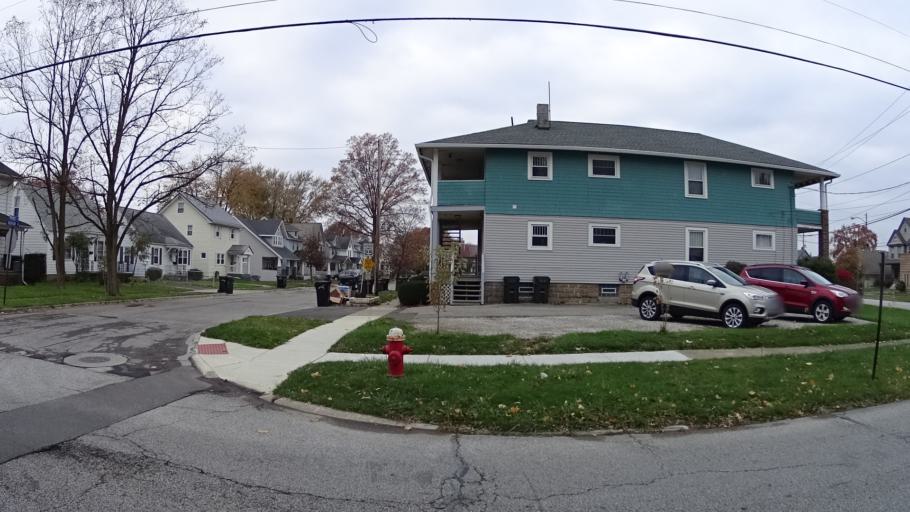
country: US
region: Ohio
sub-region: Lorain County
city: Elyria
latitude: 41.3667
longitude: -82.0887
